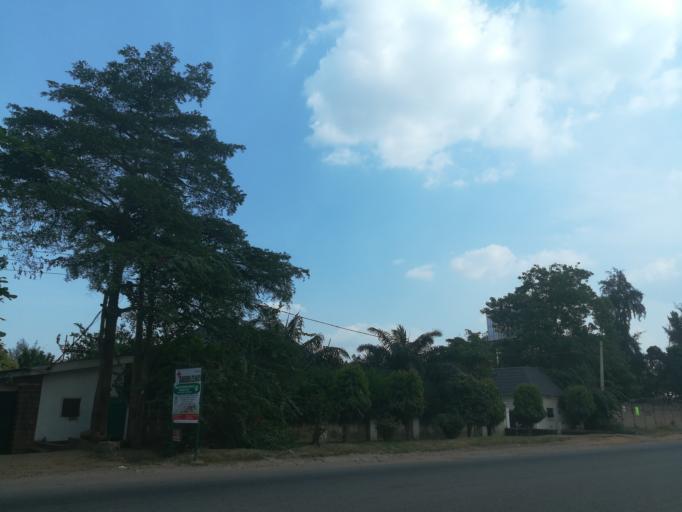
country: NG
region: Abuja Federal Capital Territory
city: Abuja
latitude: 9.0836
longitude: 7.4160
